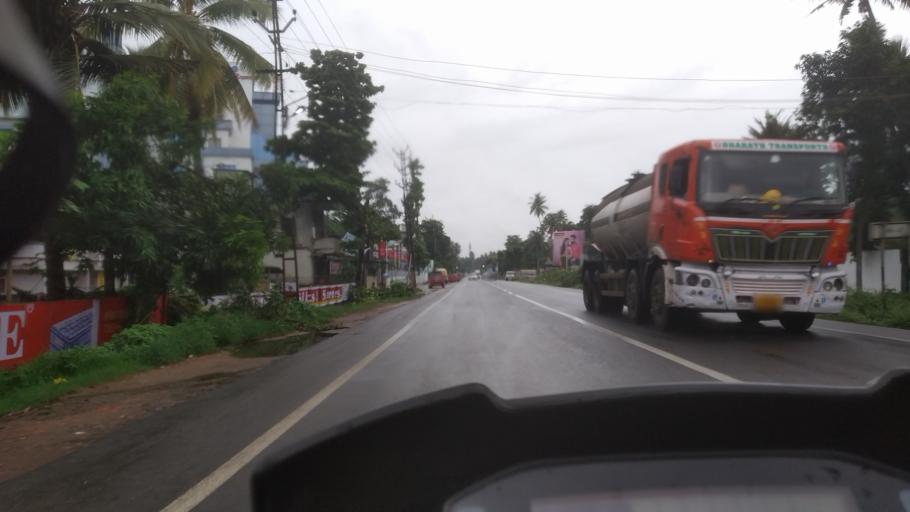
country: IN
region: Kerala
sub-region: Alappuzha
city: Kayankulam
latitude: 9.1303
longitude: 76.5150
